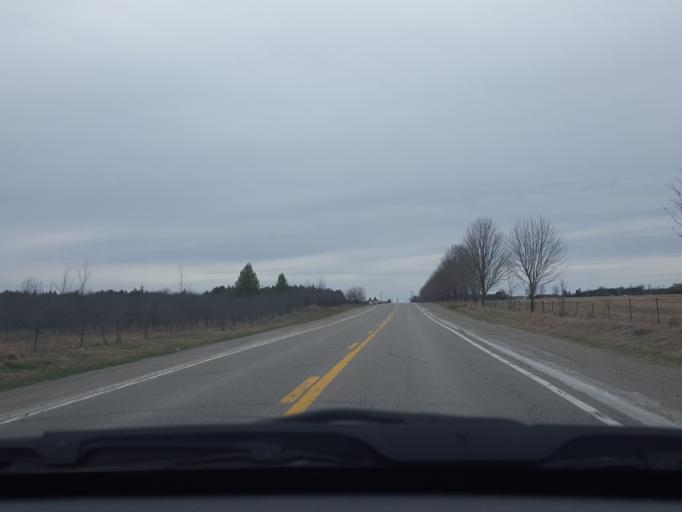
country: CA
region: Ontario
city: Uxbridge
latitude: 44.3104
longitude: -79.1769
